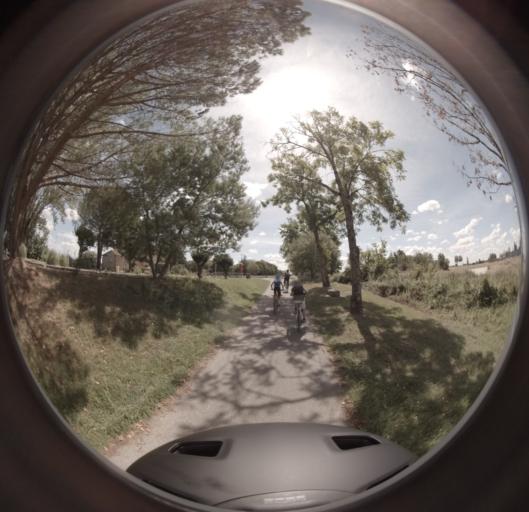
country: FR
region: Midi-Pyrenees
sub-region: Departement du Tarn-et-Garonne
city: Moissac
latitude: 44.0711
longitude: 1.0997
